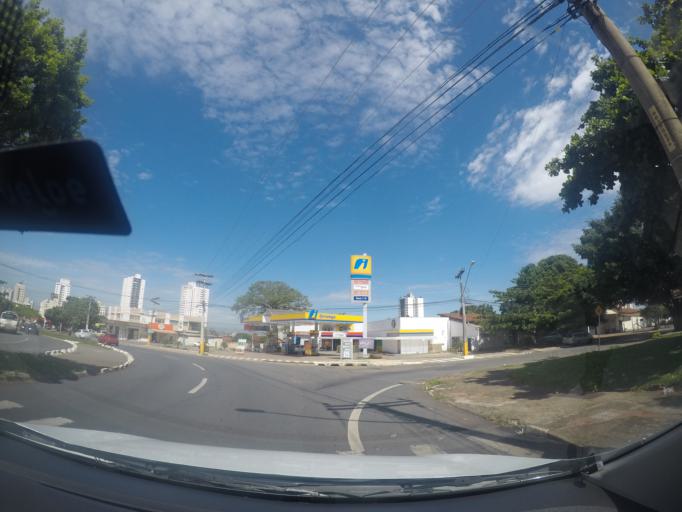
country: BR
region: Goias
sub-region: Goiania
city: Goiania
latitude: -16.7232
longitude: -49.2693
